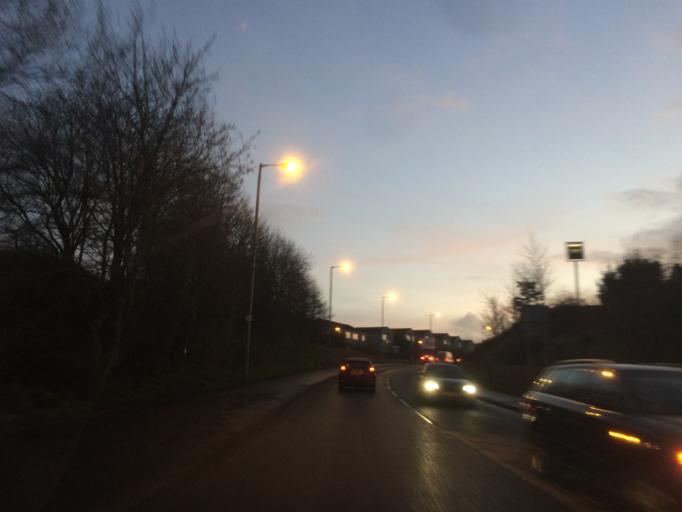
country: GB
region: Scotland
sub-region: East Renfrewshire
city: Newton Mearns
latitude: 55.7857
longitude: -4.3434
